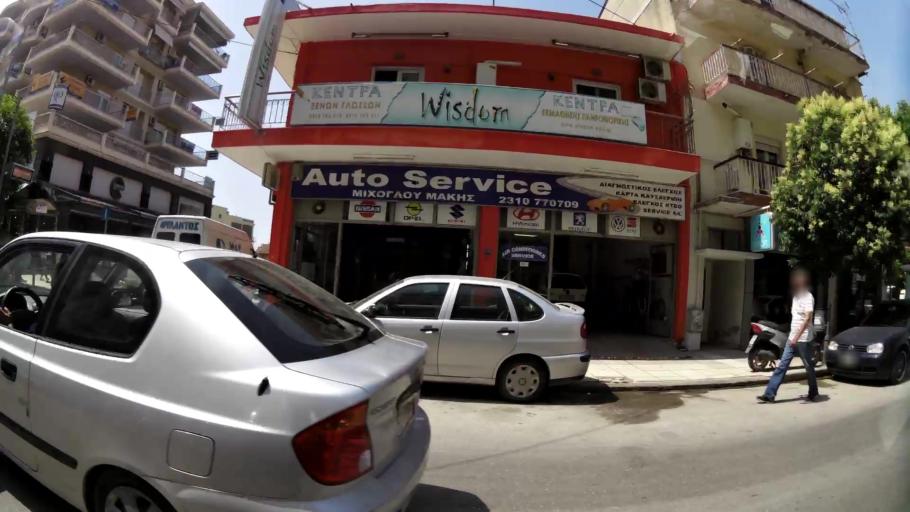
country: GR
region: Central Macedonia
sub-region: Nomos Thessalonikis
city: Evosmos
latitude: 40.6684
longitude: 22.9119
